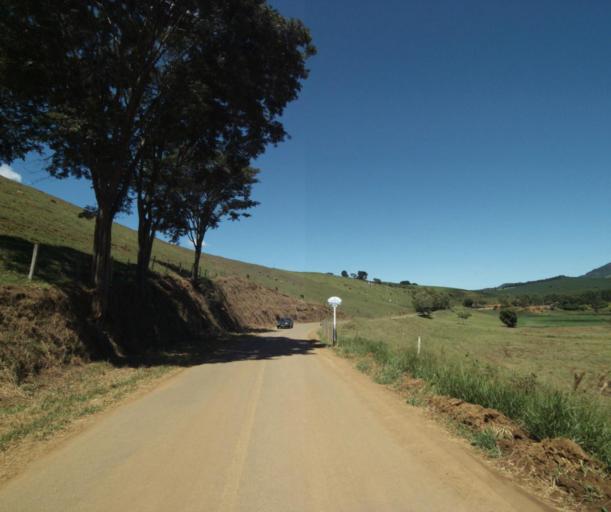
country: BR
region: Minas Gerais
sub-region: Espera Feliz
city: Espera Feliz
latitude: -20.5749
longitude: -41.8309
